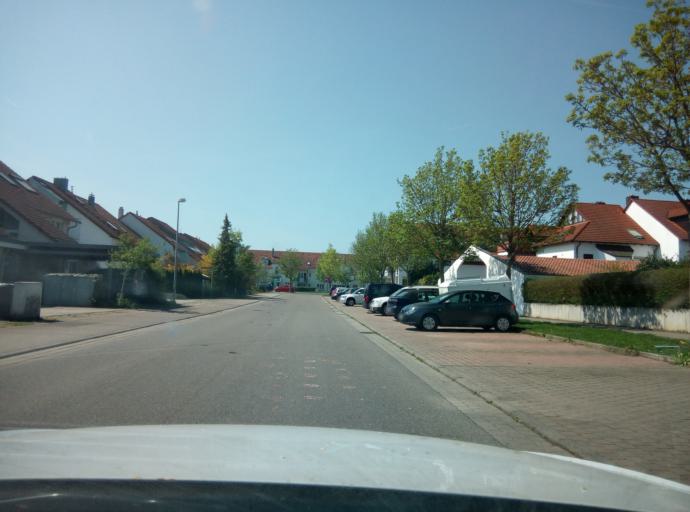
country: DE
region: Baden-Wuerttemberg
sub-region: Tuebingen Region
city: Kusterdingen
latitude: 48.5330
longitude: 9.0923
